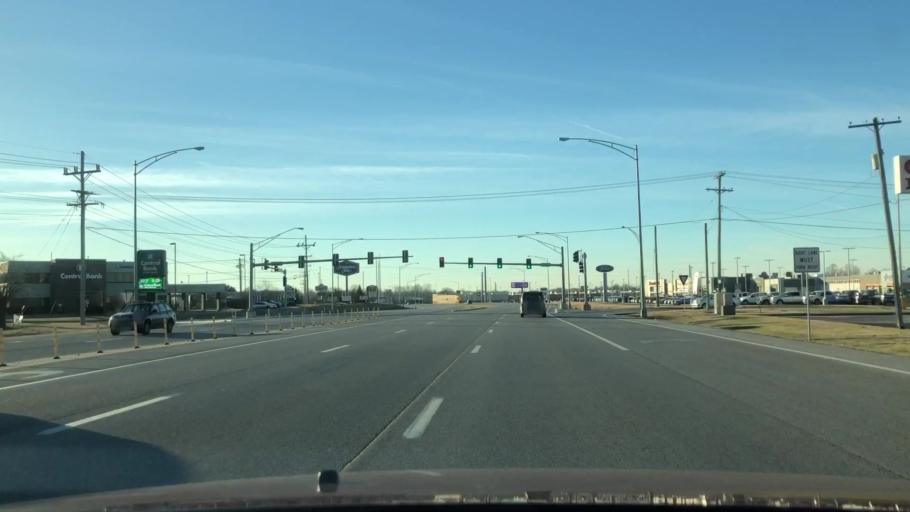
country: US
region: Missouri
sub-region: Greene County
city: Springfield
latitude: 37.1572
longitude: -93.2629
